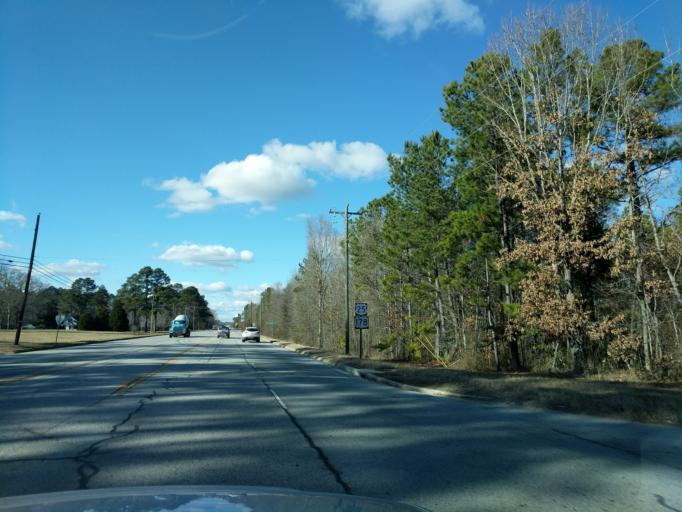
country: US
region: South Carolina
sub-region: Greenwood County
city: Greenwood
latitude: 34.1168
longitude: -82.1117
